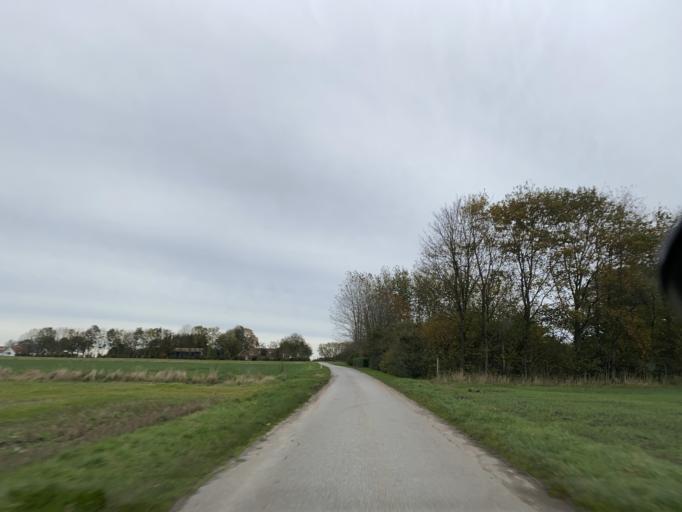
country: DK
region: Central Jutland
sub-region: Skanderborg Kommune
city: Ry
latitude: 56.1867
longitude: 9.7767
